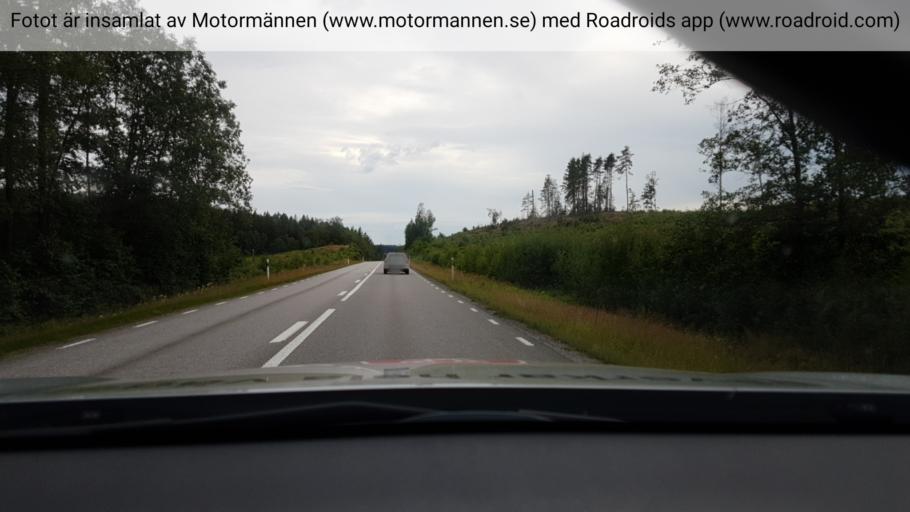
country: SE
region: Vaestra Goetaland
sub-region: Bengtsfors Kommun
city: Billingsfors
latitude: 58.9530
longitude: 12.2254
